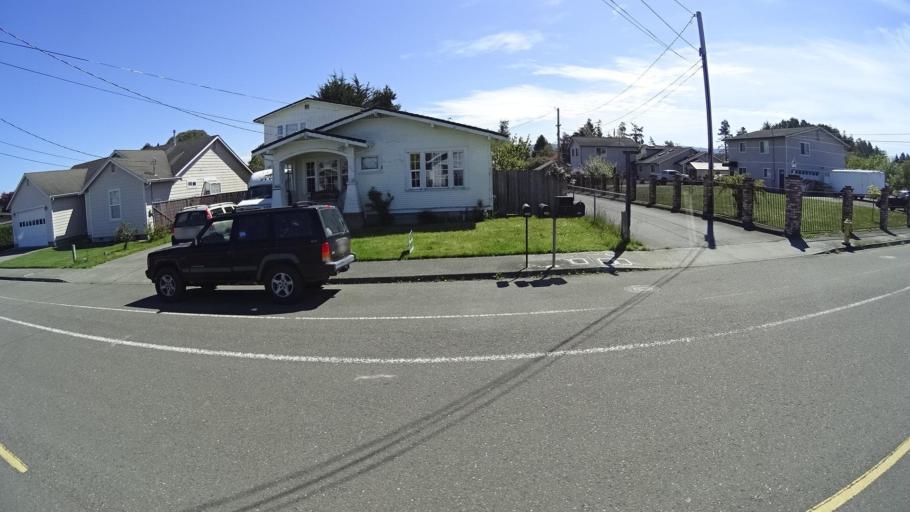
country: US
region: California
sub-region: Humboldt County
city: Myrtletown
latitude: 40.7886
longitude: -124.1263
